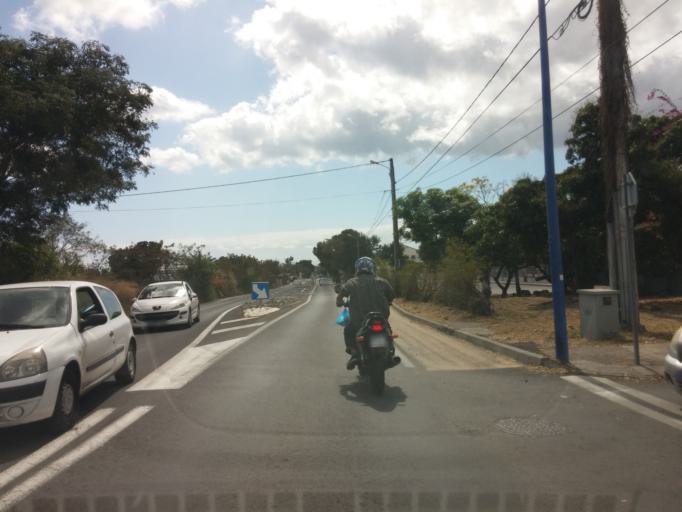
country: RE
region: Reunion
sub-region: Reunion
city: La Possession
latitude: -20.9501
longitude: 55.3259
